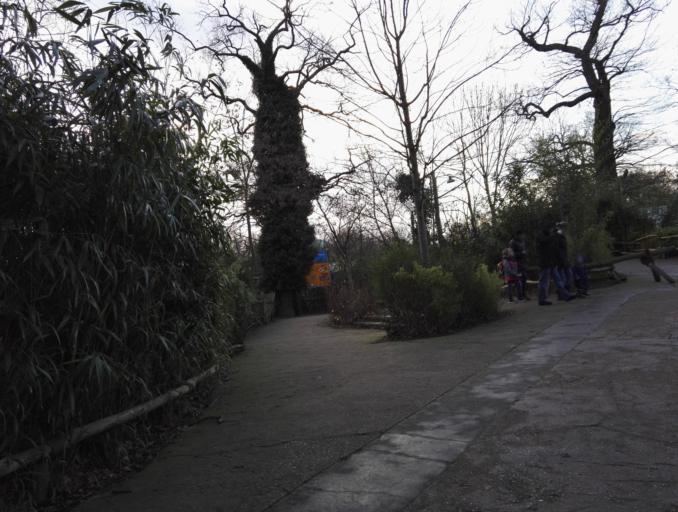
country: DE
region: Lower Saxony
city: Hannover
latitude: 52.3809
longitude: 9.7693
